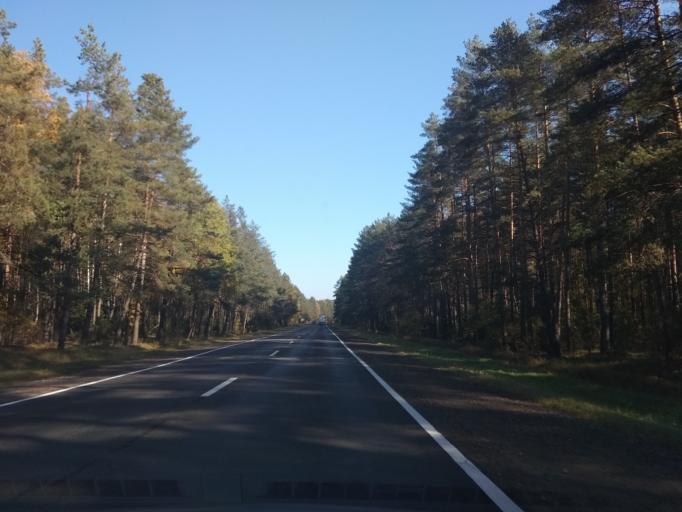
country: BY
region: Brest
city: Baranovichi
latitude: 53.0439
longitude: 25.8194
